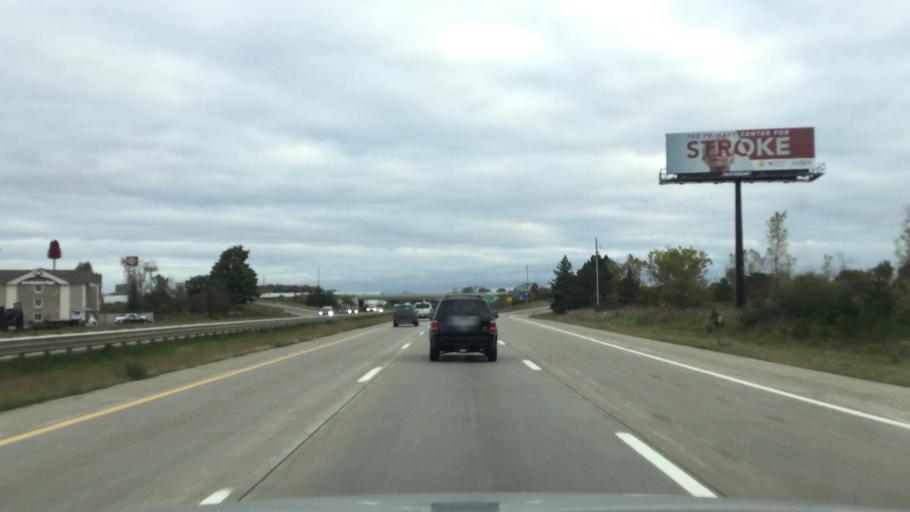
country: US
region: Michigan
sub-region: Genesee County
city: Flint
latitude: 42.9408
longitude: -83.7235
